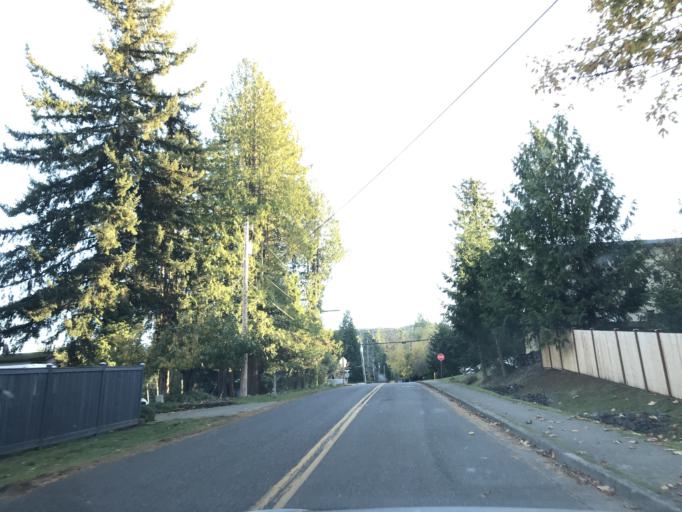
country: US
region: Washington
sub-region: Whatcom County
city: Geneva
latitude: 48.7469
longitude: -122.4044
